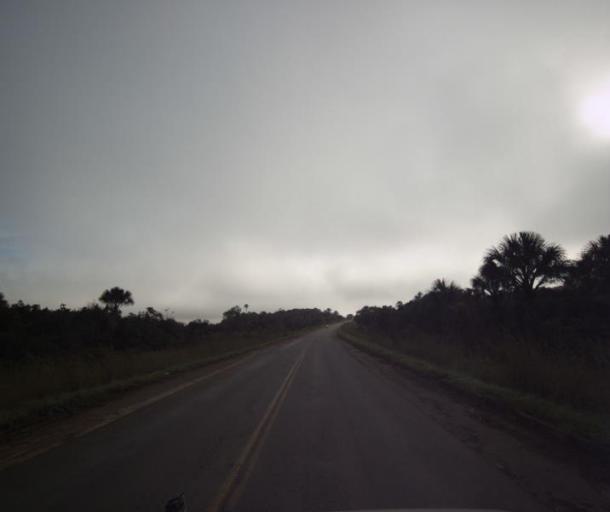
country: BR
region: Goias
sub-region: Pirenopolis
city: Pirenopolis
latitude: -15.7621
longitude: -48.7567
